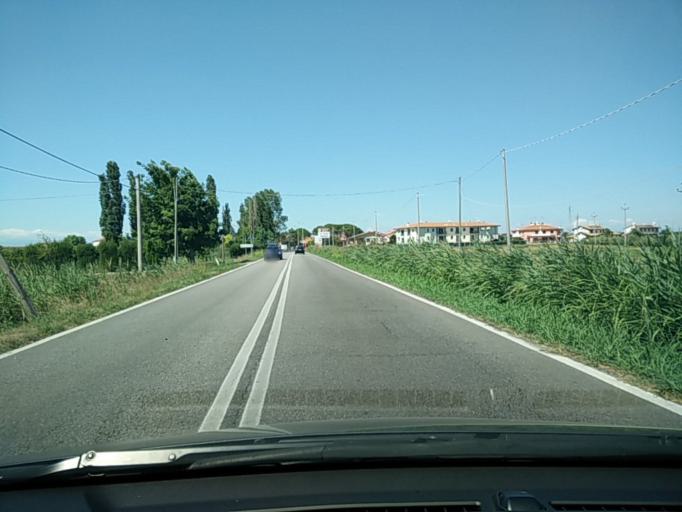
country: IT
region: Veneto
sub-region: Provincia di Venezia
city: La Salute di Livenza
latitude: 45.6426
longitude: 12.8434
